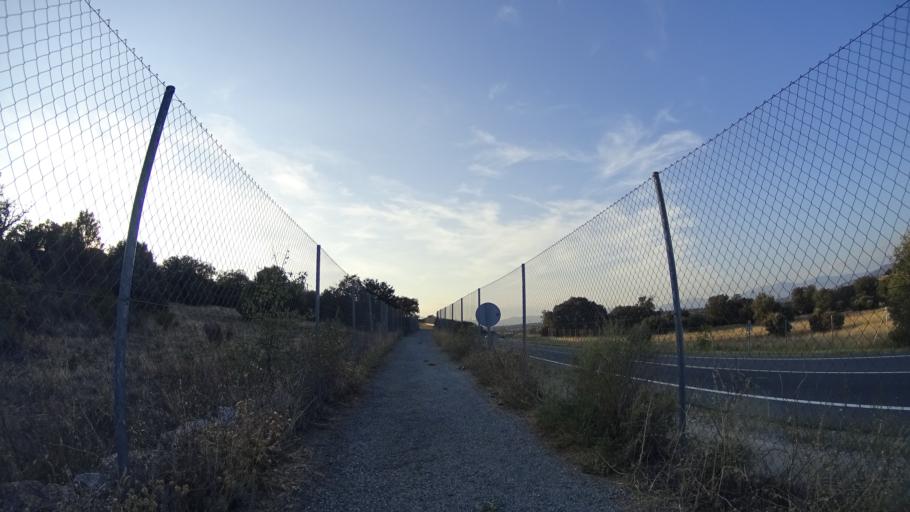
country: ES
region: Madrid
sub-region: Provincia de Madrid
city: Galapagar
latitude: 40.5720
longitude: -3.9844
